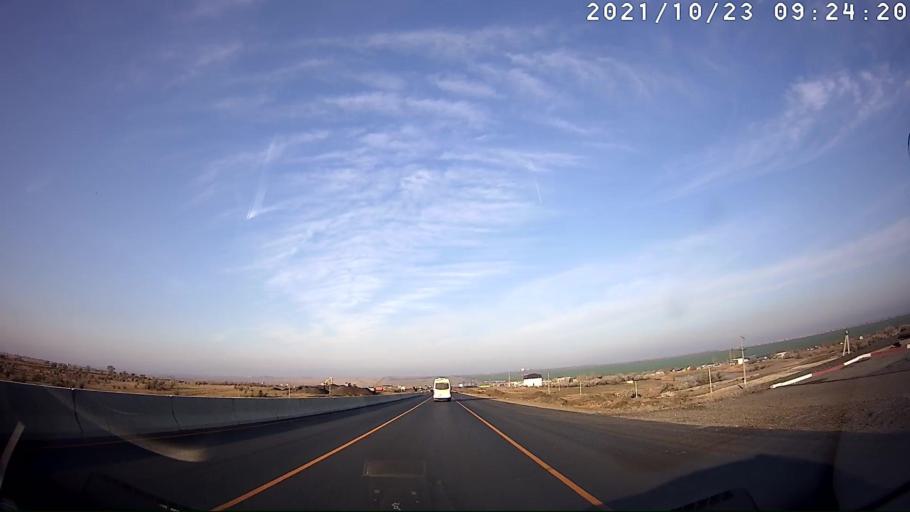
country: RU
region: Saratov
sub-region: Saratovskiy Rayon
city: Saratov
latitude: 51.6700
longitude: 45.9914
